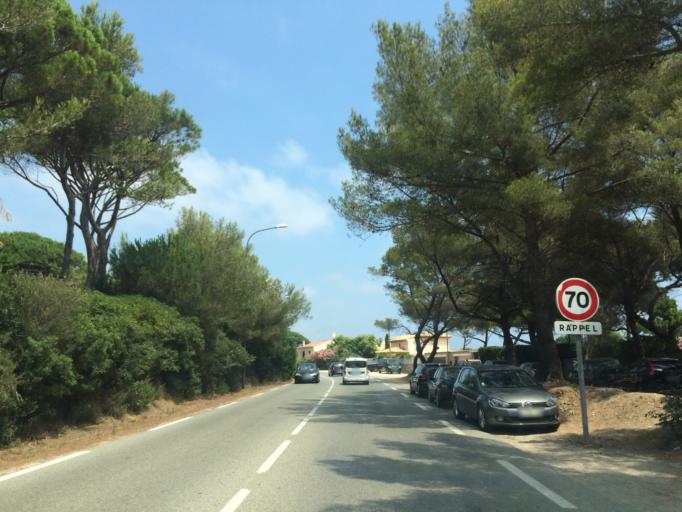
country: FR
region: Provence-Alpes-Cote d'Azur
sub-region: Departement du Var
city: Sainte-Maxime
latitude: 43.3257
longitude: 6.6655
